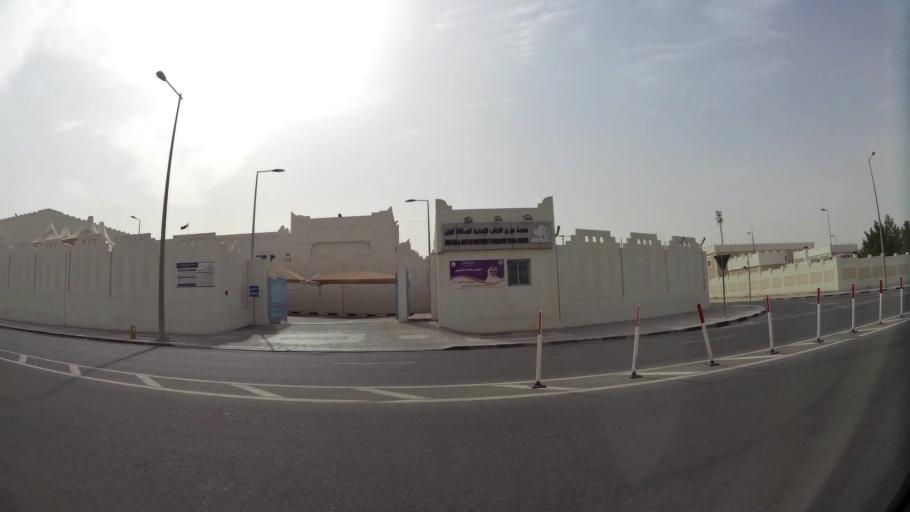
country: QA
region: Baladiyat ad Dawhah
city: Doha
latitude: 25.3207
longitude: 51.5067
